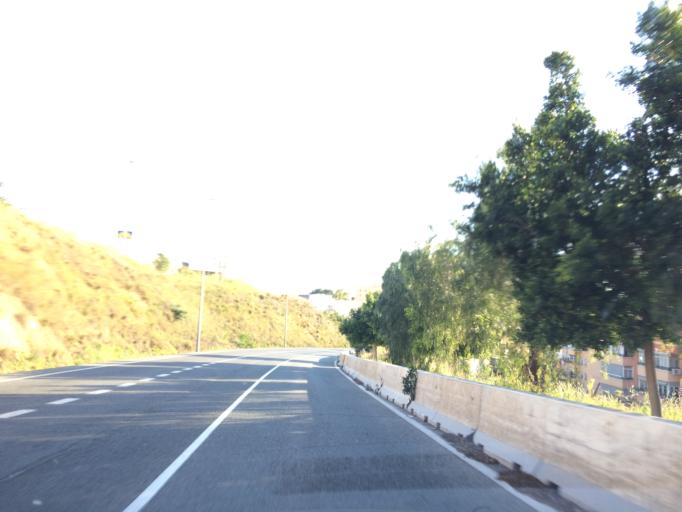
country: ES
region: Andalusia
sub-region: Provincia de Malaga
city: Malaga
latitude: 36.7384
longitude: -4.4182
